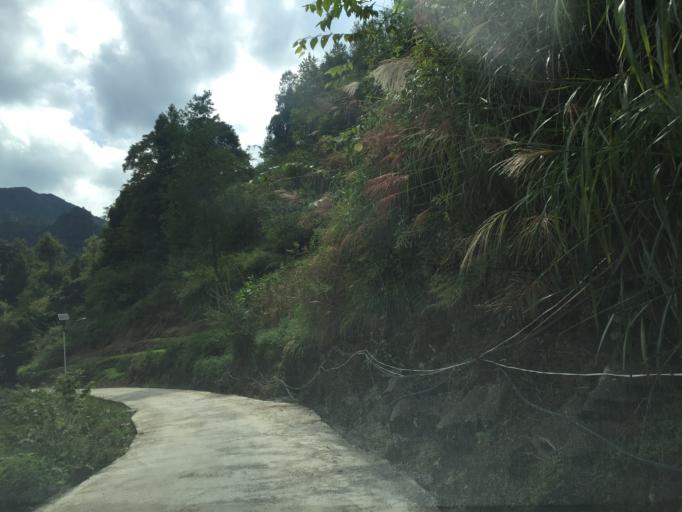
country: CN
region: Guizhou Sheng
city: Quankou
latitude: 28.5438
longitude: 108.1233
